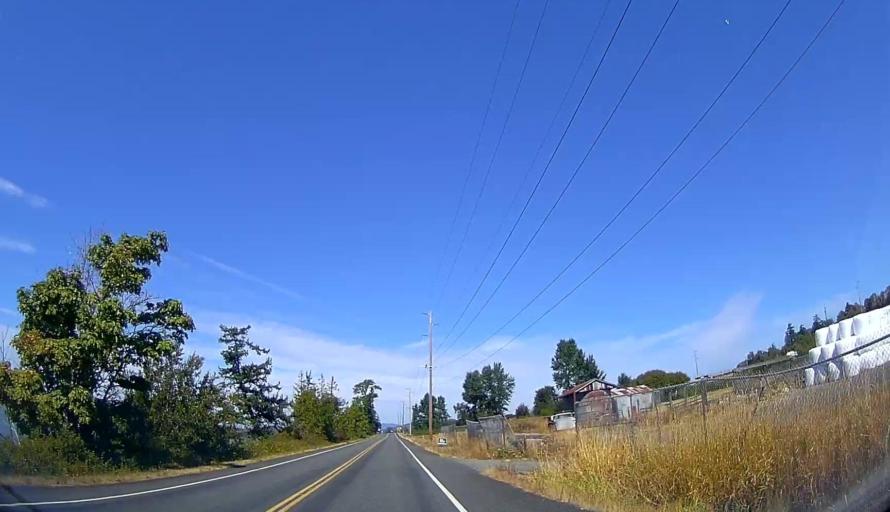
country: US
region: Washington
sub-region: Skagit County
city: Anacortes
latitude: 48.4740
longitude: -122.5715
